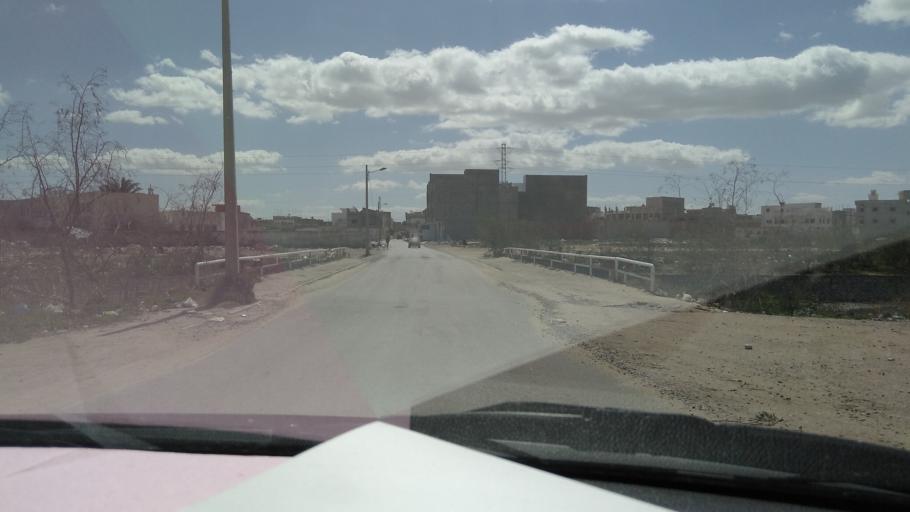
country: TN
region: Al Qayrawan
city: Kairouan
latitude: 35.6647
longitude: 10.1089
